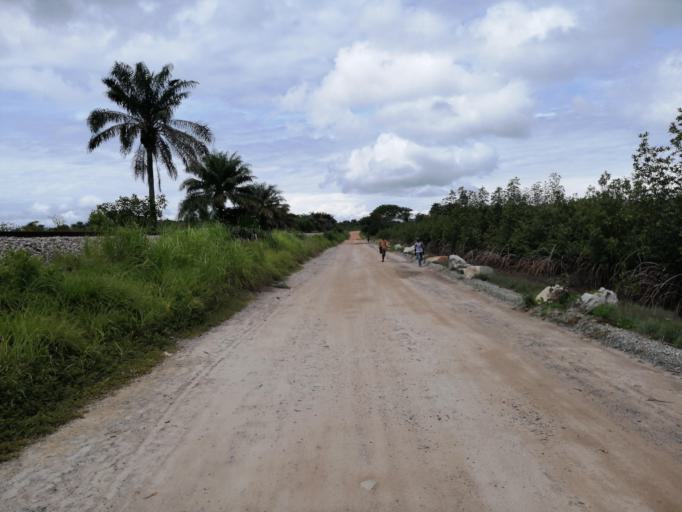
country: SL
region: Northern Province
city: Pepel
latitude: 8.6051
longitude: -13.0519
